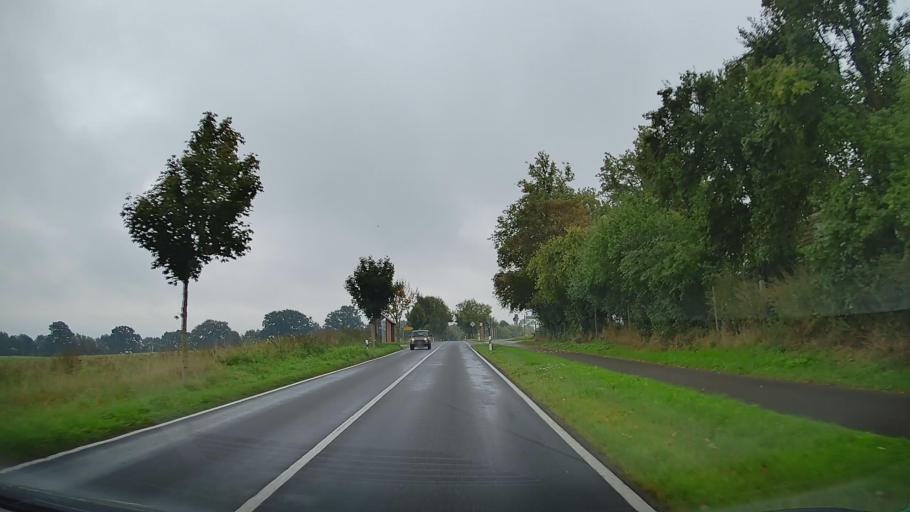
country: DE
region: Mecklenburg-Vorpommern
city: Ostseebad Boltenhagen
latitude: 53.9436
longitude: 11.2378
